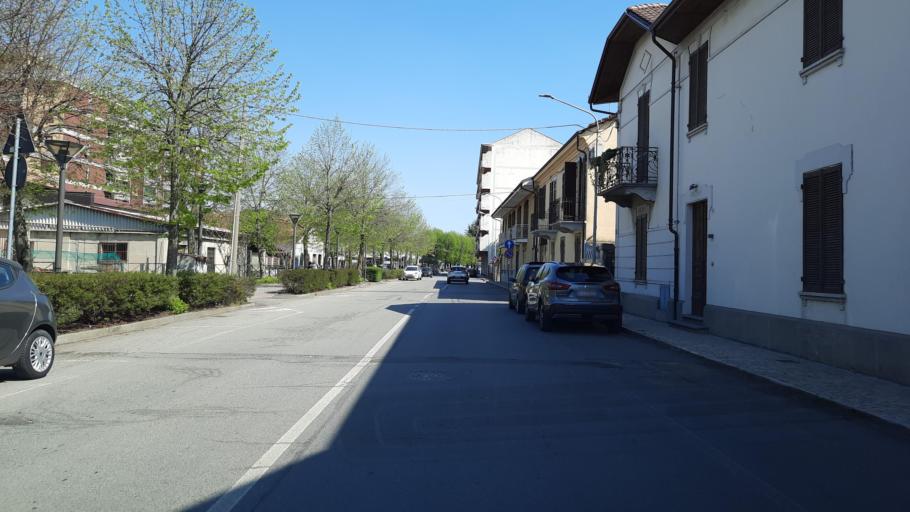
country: IT
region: Piedmont
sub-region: Provincia di Vercelli
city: Crescentino
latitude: 45.1907
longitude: 8.0998
